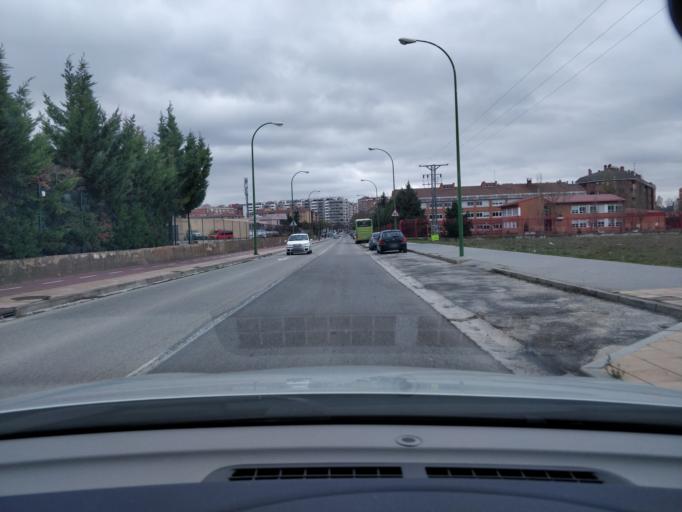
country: ES
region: Castille and Leon
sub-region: Provincia de Burgos
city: Burgos
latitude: 42.3600
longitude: -3.6602
